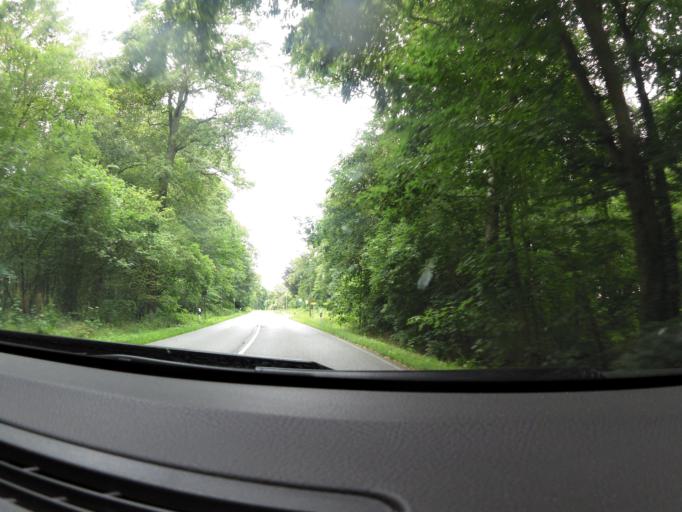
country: DE
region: North Rhine-Westphalia
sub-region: Regierungsbezirk Dusseldorf
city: Sonsbeck
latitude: 51.6132
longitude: 6.4102
